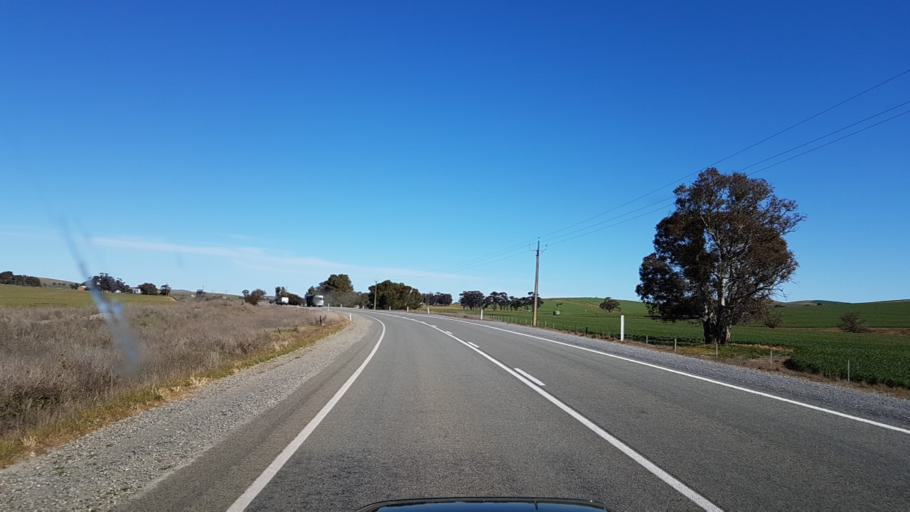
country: AU
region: South Australia
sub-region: Clare and Gilbert Valleys
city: Clare
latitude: -33.6105
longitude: 138.8936
